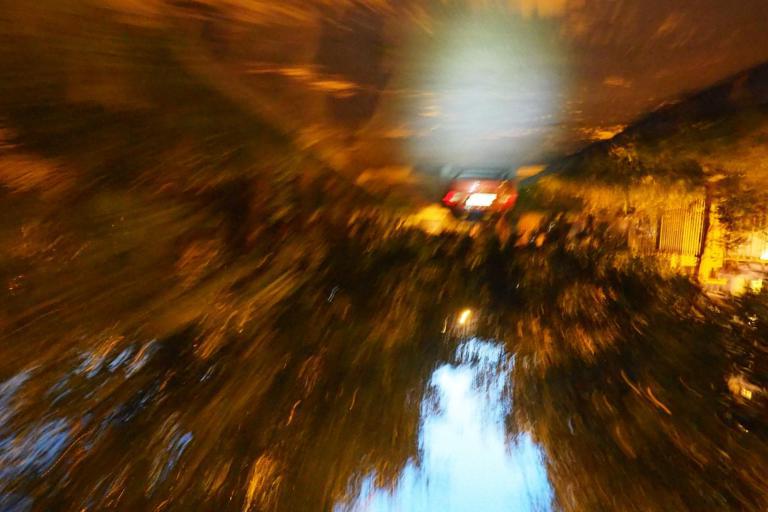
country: RU
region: Moscow
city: Ramenki
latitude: 55.6974
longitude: 37.5080
